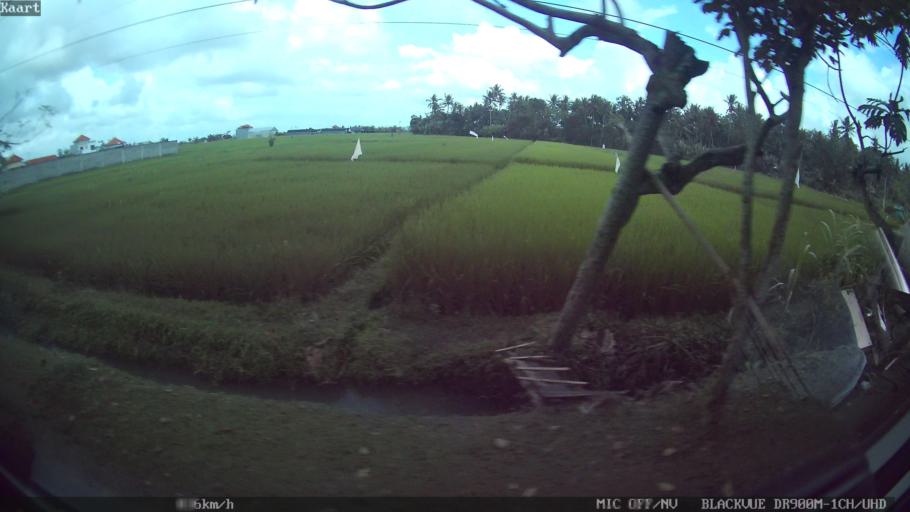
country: ID
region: Bali
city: Banjar Bucu
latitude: -8.5758
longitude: 115.2033
